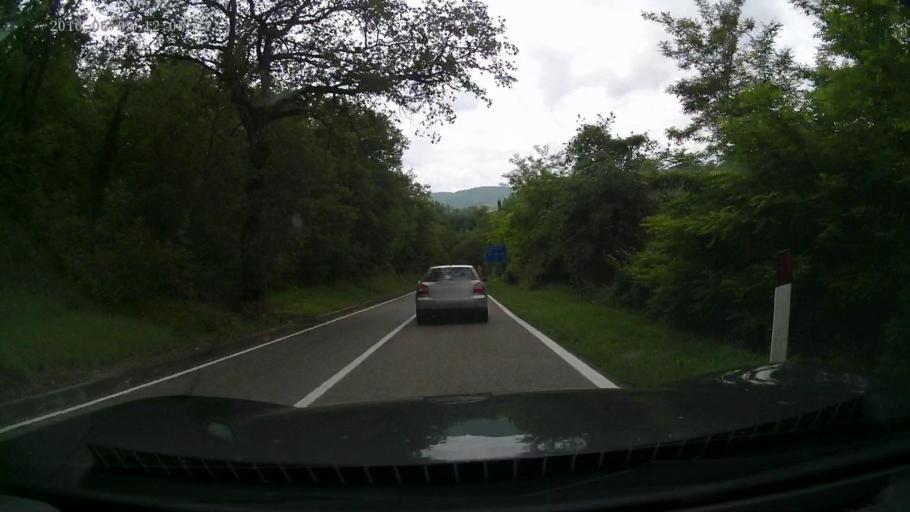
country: IT
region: Tuscany
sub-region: Province of Florence
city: Panzano in Chianti
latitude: 43.5211
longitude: 11.2942
